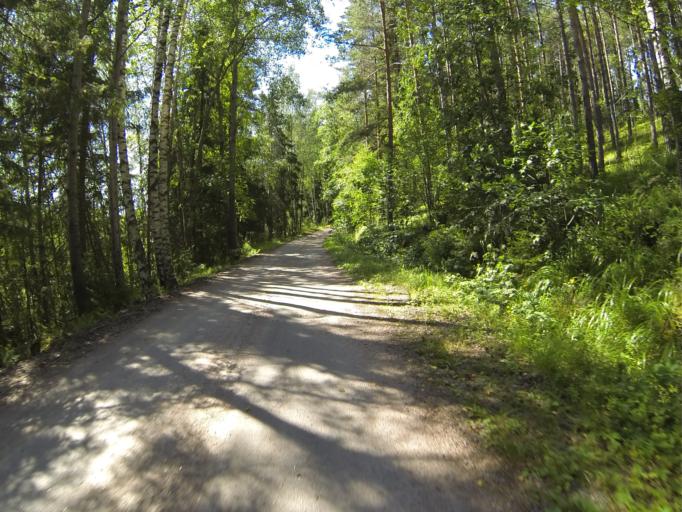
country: FI
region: Varsinais-Suomi
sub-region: Salo
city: Pernioe
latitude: 60.2893
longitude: 23.0810
